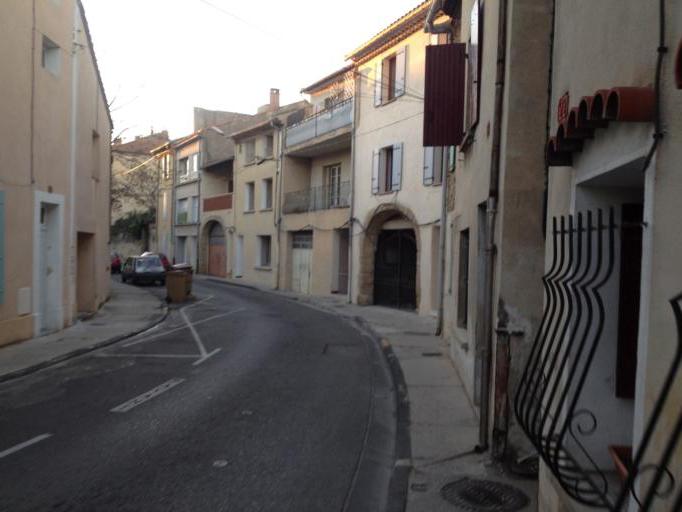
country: FR
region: Provence-Alpes-Cote d'Azur
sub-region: Departement du Vaucluse
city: Orange
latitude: 44.1398
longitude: 4.8079
